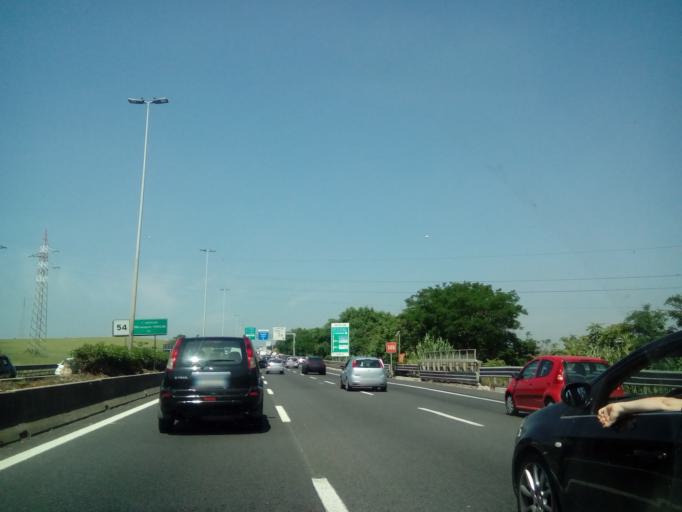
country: IT
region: Latium
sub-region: Citta metropolitana di Roma Capitale
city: Selcetta
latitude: 41.7996
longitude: 12.4640
